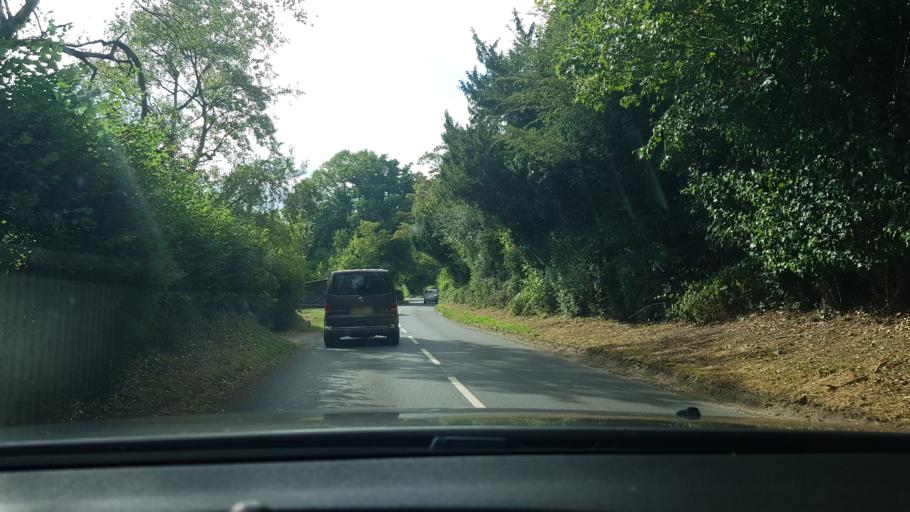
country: GB
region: England
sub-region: West Berkshire
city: Hermitage
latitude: 51.4658
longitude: -1.1976
